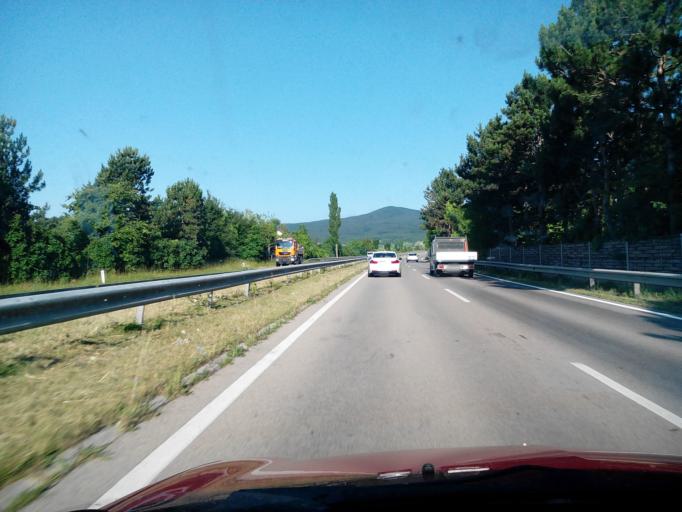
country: AT
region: Lower Austria
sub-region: Politischer Bezirk Baden
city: Baden
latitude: 47.9941
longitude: 16.2428
